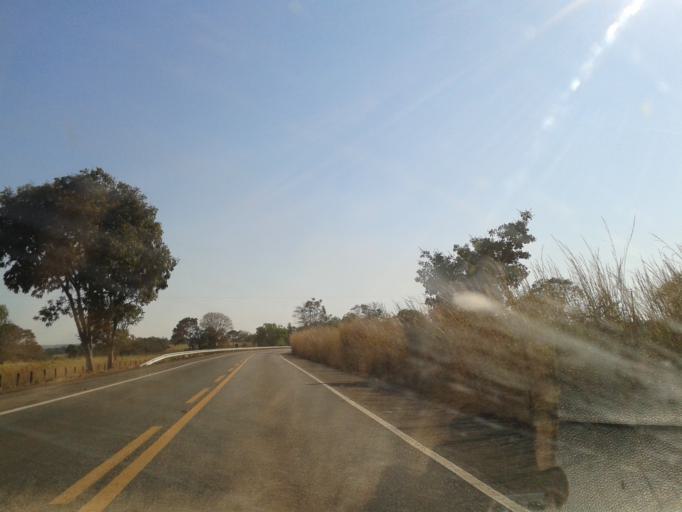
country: BR
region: Goias
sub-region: Mozarlandia
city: Mozarlandia
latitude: -14.8736
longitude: -50.5520
